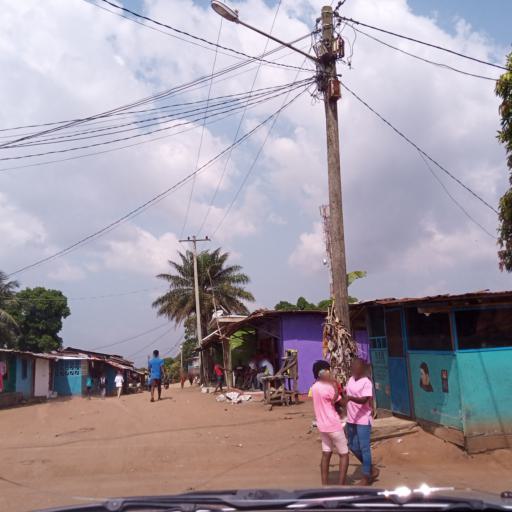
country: LR
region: Montserrado
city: Monrovia
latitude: 6.2922
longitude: -10.7658
